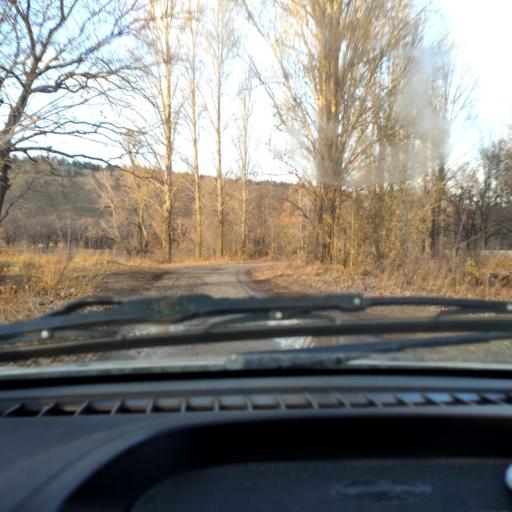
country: RU
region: Samara
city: Povolzhskiy
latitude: 53.4672
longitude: 49.6863
